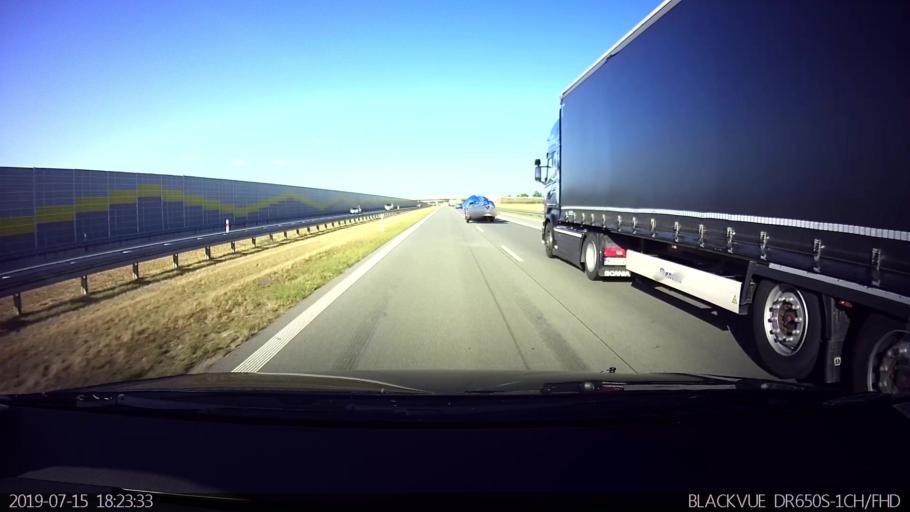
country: PL
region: Lodz Voivodeship
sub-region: Powiat laski
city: Lask
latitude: 51.5617
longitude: 19.1341
